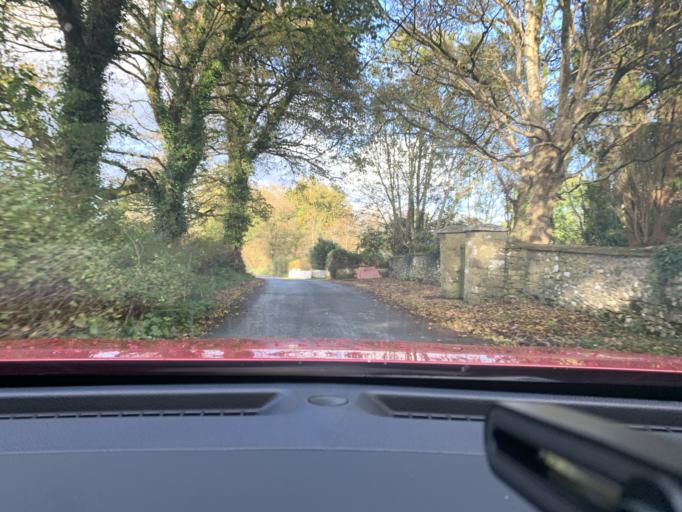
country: IE
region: Connaught
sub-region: Sligo
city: Ballymote
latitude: 54.0986
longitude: -8.4358
